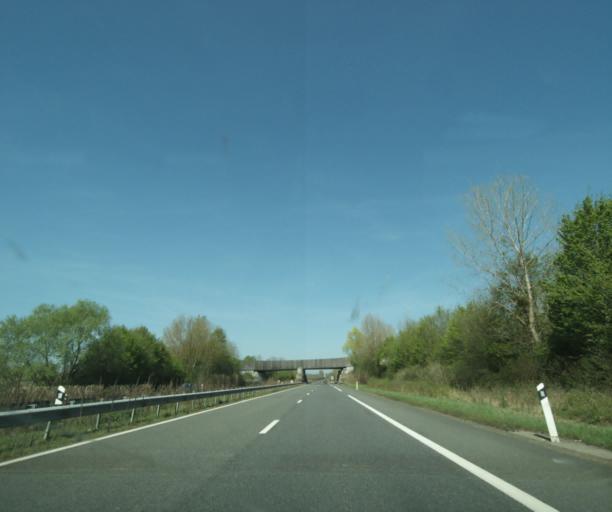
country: FR
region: Bourgogne
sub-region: Departement de la Nievre
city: La Charite-sur-Loire
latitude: 47.2183
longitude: 3.0052
